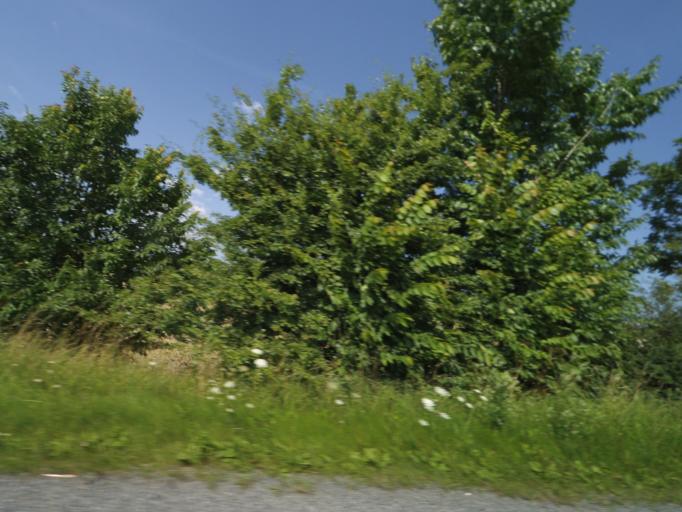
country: DK
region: South Denmark
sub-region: Assens Kommune
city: Vissenbjerg
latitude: 55.3967
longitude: 10.0976
